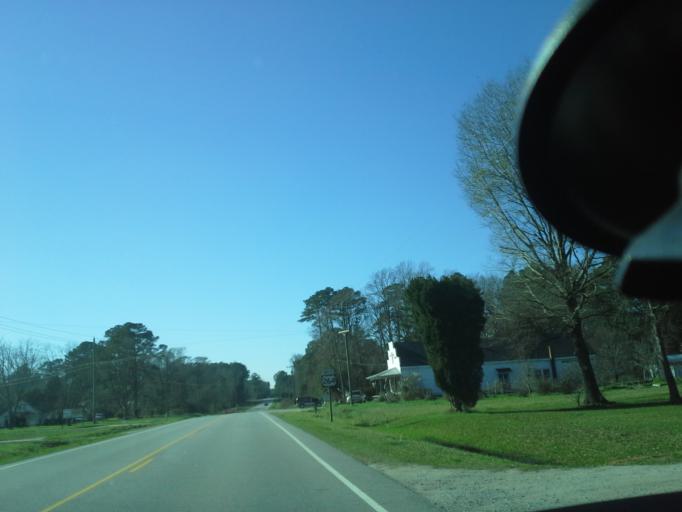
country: US
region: North Carolina
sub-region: Beaufort County
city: Belhaven
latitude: 35.5235
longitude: -76.8061
